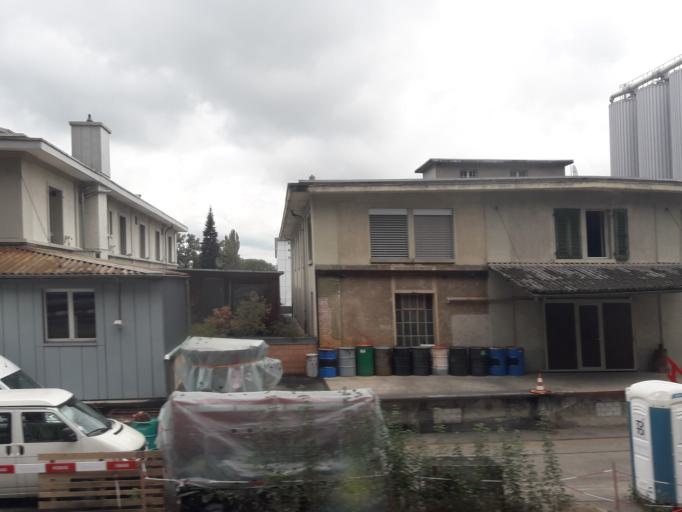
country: CH
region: Bern
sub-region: Bern-Mittelland District
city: Bern
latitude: 46.9266
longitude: 7.4511
